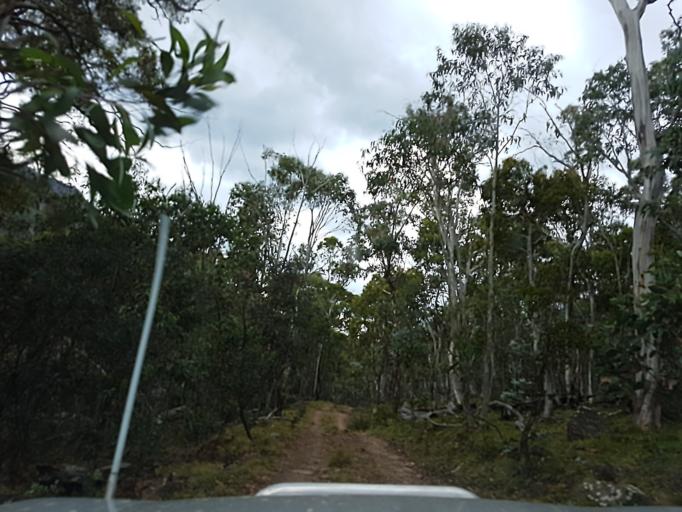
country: AU
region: New South Wales
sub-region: Snowy River
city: Jindabyne
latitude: -36.8835
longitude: 148.1482
